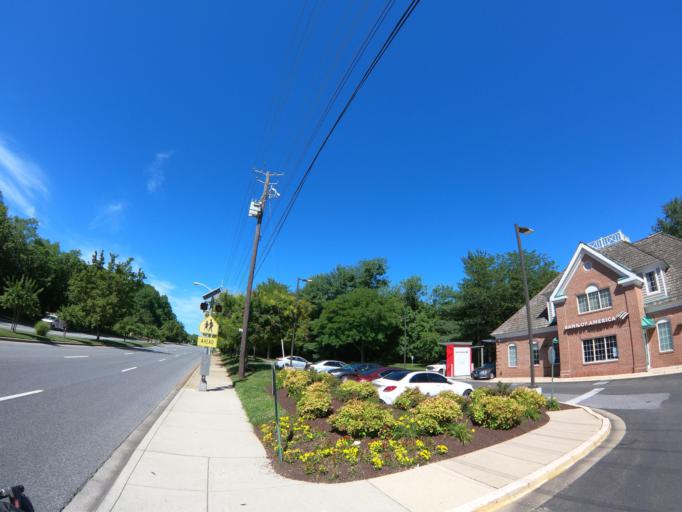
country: US
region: Maryland
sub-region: Prince George's County
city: Lake Arbor
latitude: 38.9055
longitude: -76.8293
